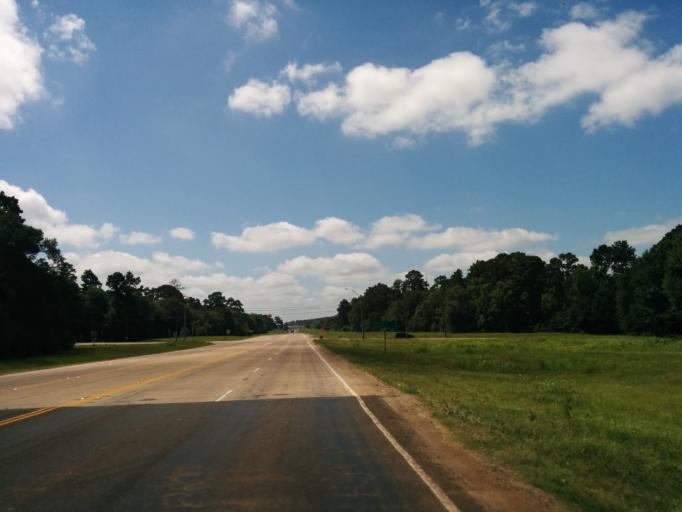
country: US
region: Texas
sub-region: Houston County
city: Crockett
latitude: 31.3125
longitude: -95.4784
